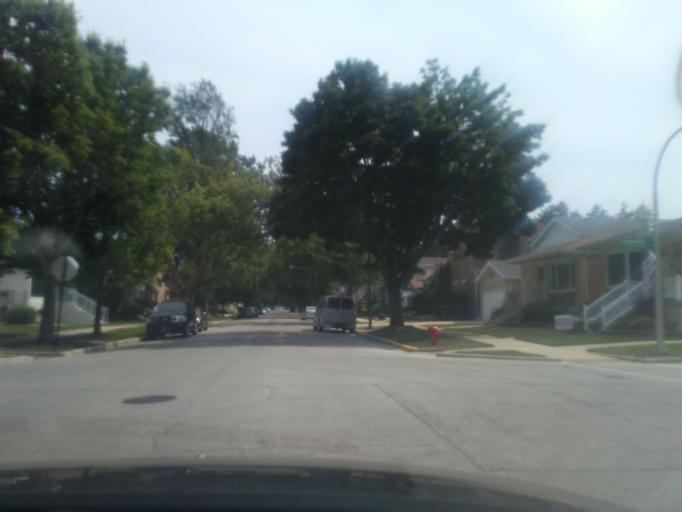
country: US
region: Illinois
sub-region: Cook County
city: Harwood Heights
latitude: 41.9803
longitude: -87.7939
